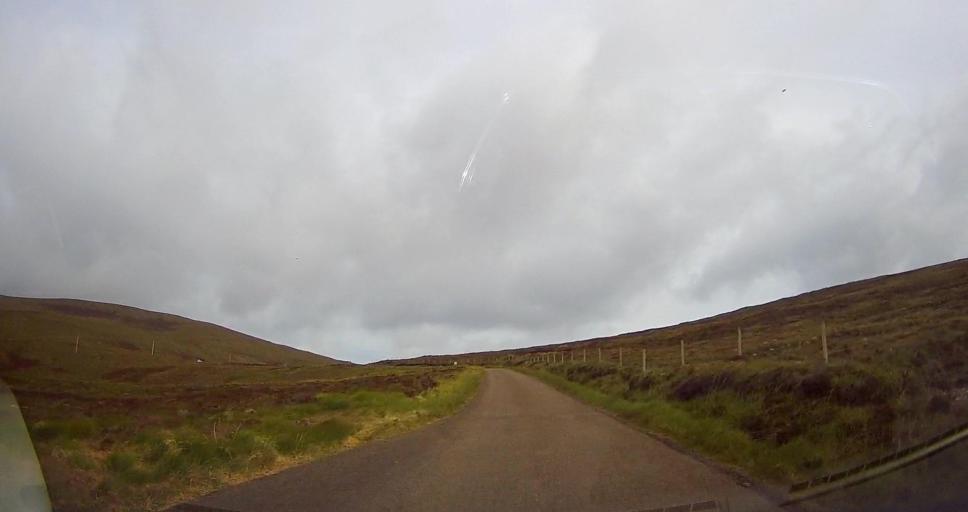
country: GB
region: Scotland
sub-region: Orkney Islands
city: Stromness
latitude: 58.8770
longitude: -3.2469
